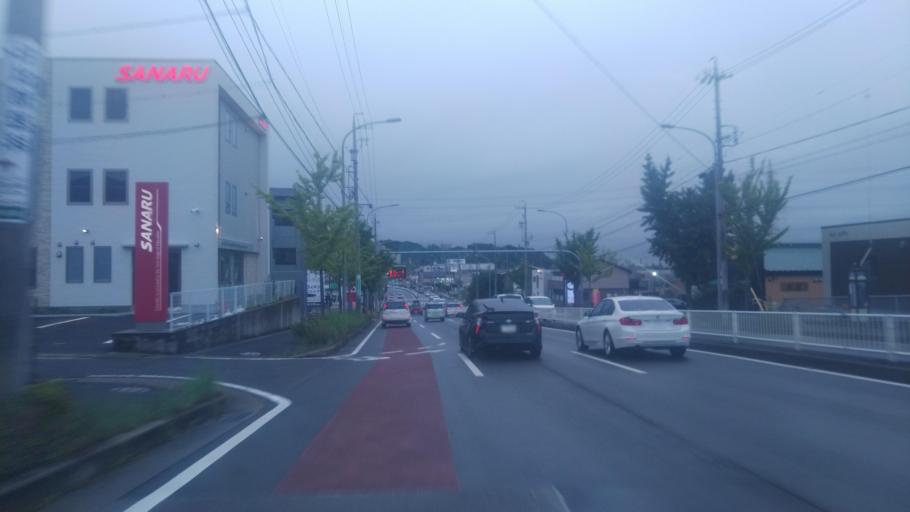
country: JP
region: Aichi
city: Kasugai
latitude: 35.2337
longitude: 136.9997
